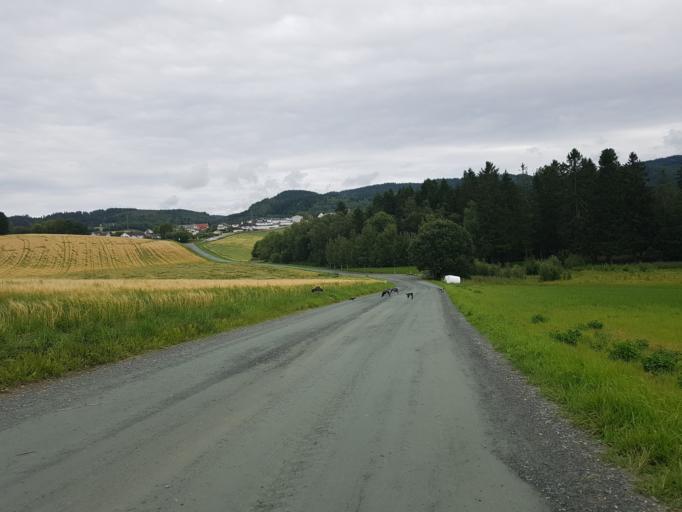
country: NO
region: Sor-Trondelag
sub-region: Trondheim
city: Trondheim
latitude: 63.3829
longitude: 10.4154
